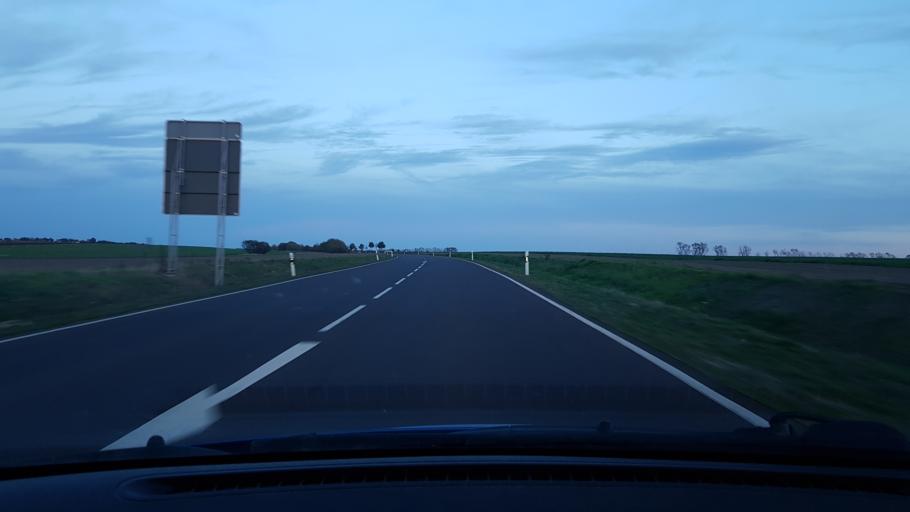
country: DE
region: Saxony-Anhalt
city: Leitzkau
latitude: 52.0491
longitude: 11.9523
